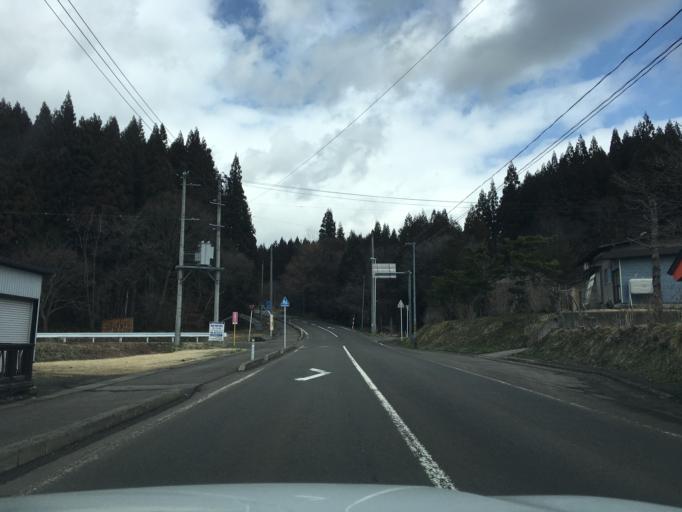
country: JP
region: Akita
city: Takanosu
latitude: 40.1632
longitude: 140.3231
